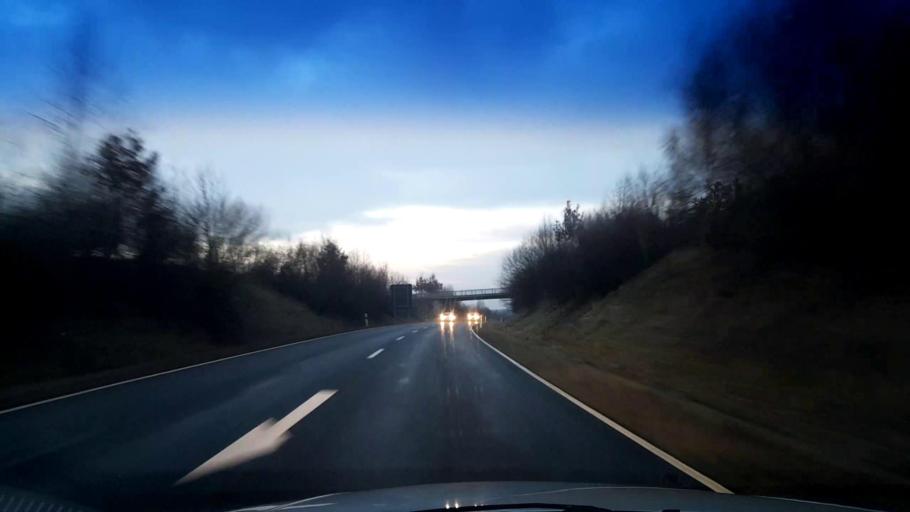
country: DE
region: Bavaria
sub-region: Upper Franconia
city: Arzberg
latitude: 50.0148
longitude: 12.2117
